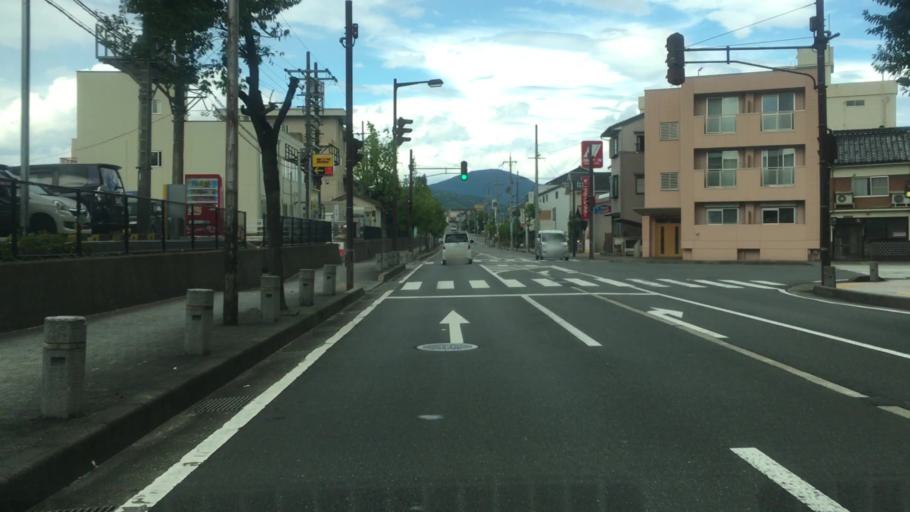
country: JP
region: Hyogo
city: Toyooka
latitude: 35.5446
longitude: 134.8141
